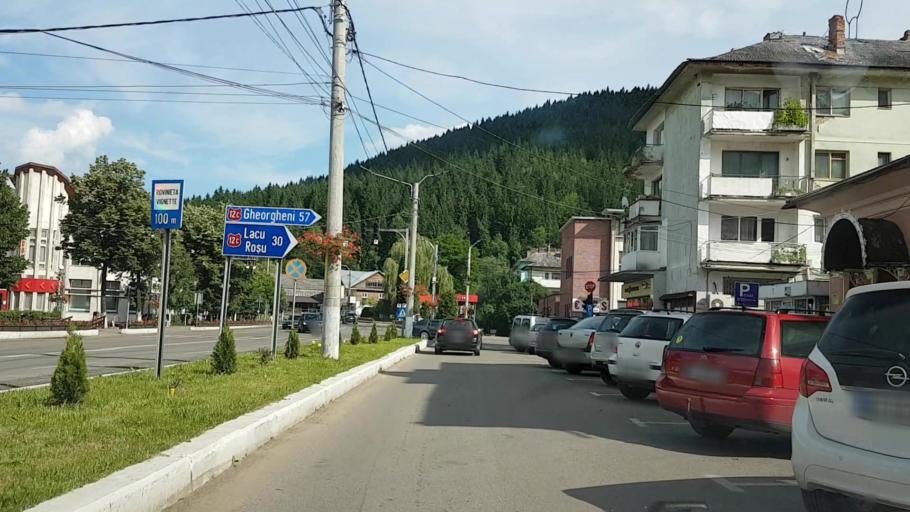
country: RO
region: Neamt
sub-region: Comuna Bicaz
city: Dodeni
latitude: 46.9119
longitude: 26.0877
